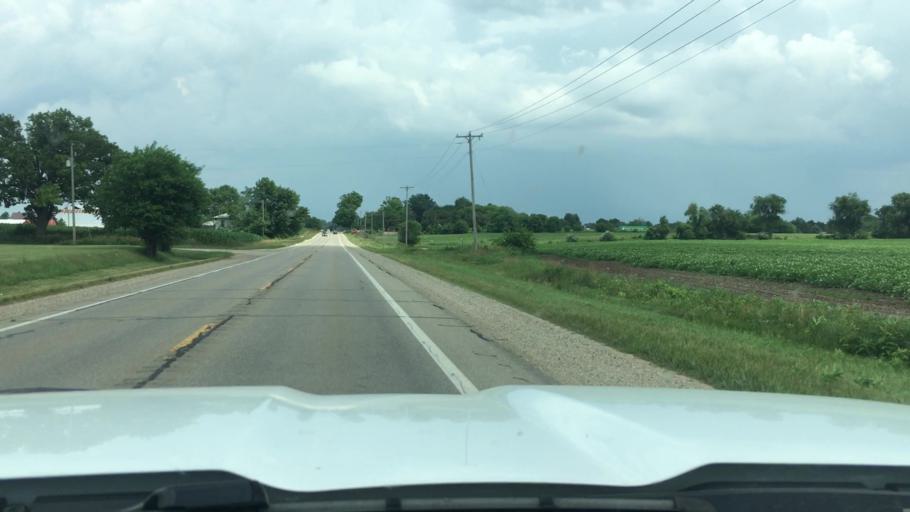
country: US
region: Michigan
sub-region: Montcalm County
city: Greenville
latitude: 43.1704
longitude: -85.2047
